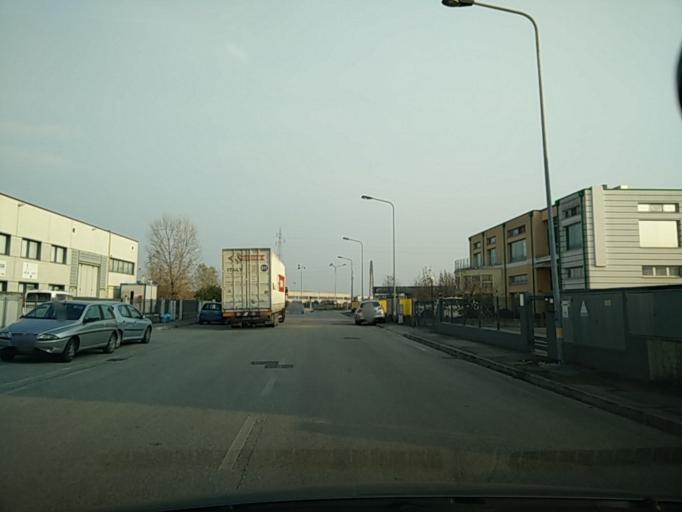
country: IT
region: Veneto
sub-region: Provincia di Treviso
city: Salvatronda
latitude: 45.6833
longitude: 11.9620
